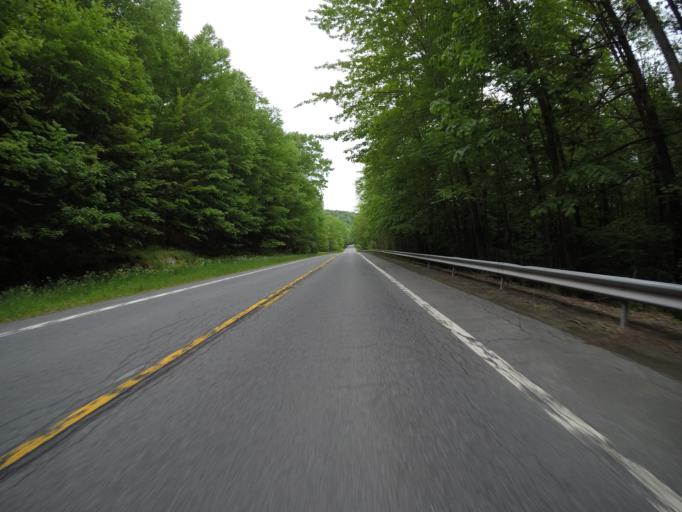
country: US
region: New York
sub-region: Sullivan County
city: Livingston Manor
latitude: 42.0747
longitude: -74.8728
